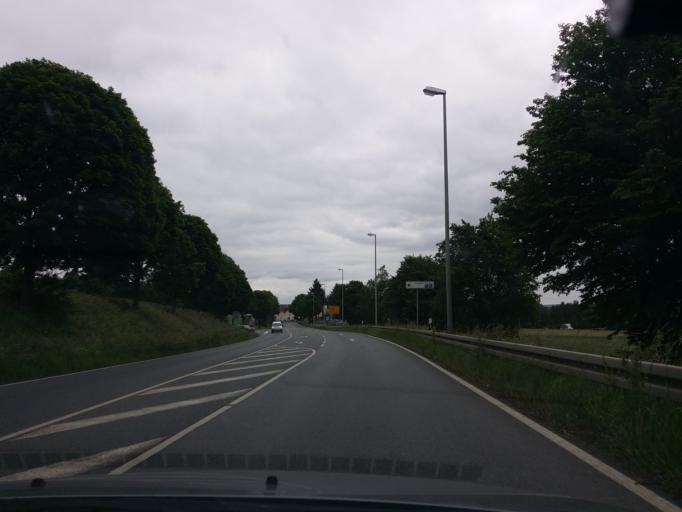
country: DE
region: Hesse
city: Bad Camberg
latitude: 50.2907
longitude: 8.2744
